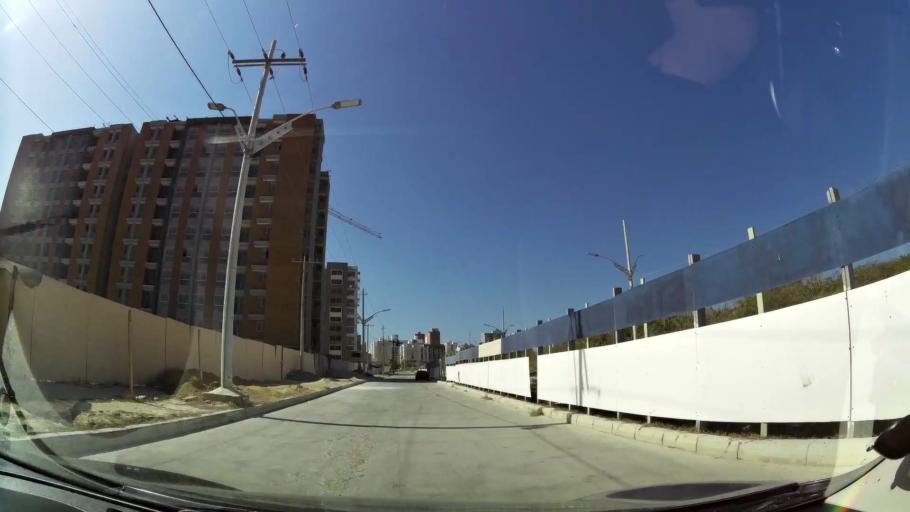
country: CO
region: Atlantico
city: Barranquilla
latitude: 11.0233
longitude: -74.8195
